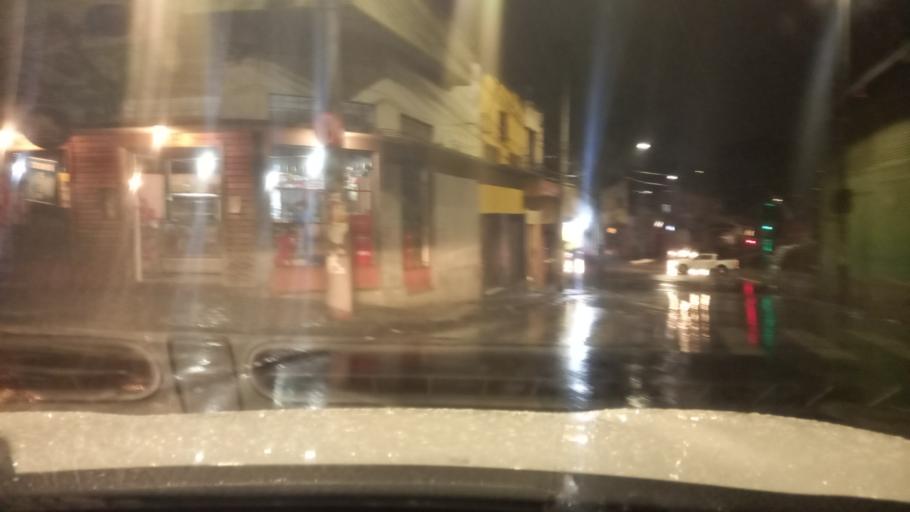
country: BR
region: Minas Gerais
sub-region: Belo Horizonte
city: Belo Horizonte
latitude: -19.9090
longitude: -43.9137
